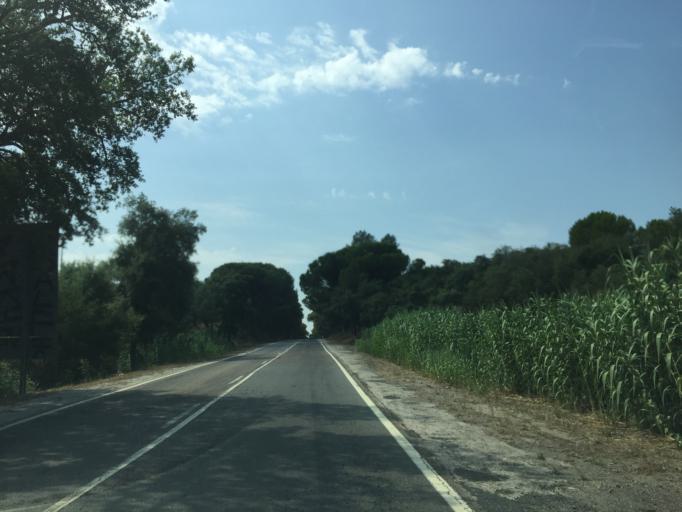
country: PT
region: Setubal
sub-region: Alcacer do Sal
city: Alcacer do Sal
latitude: 38.3381
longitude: -8.5206
